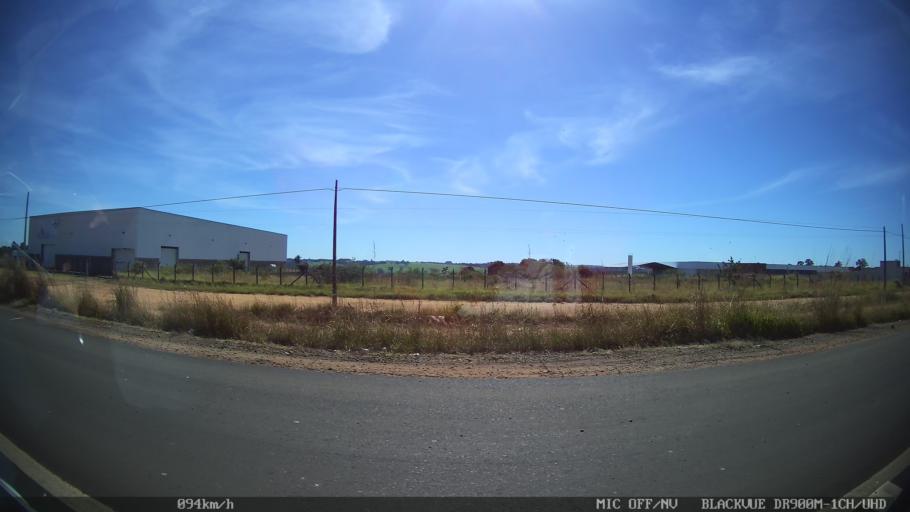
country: BR
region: Sao Paulo
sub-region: Franca
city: Franca
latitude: -20.5459
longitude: -47.4735
